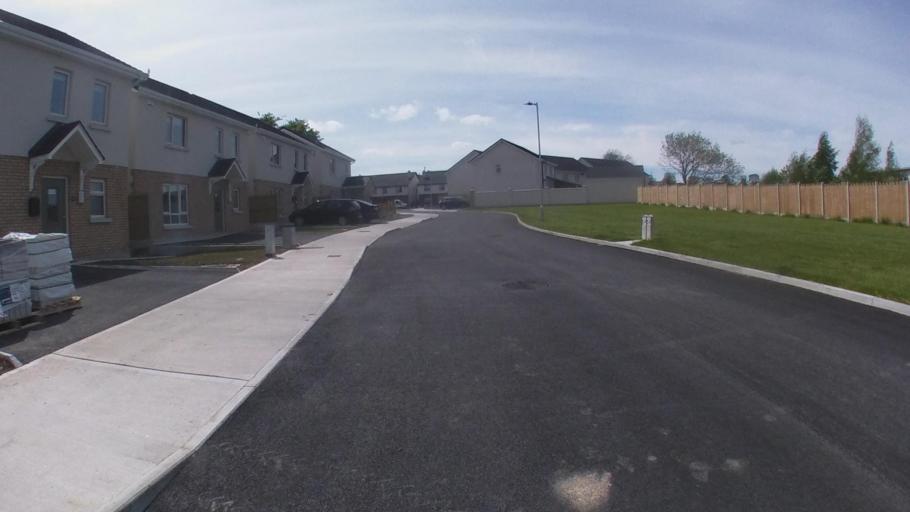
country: IE
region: Leinster
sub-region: County Carlow
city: Carlow
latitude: 52.8508
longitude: -6.9923
